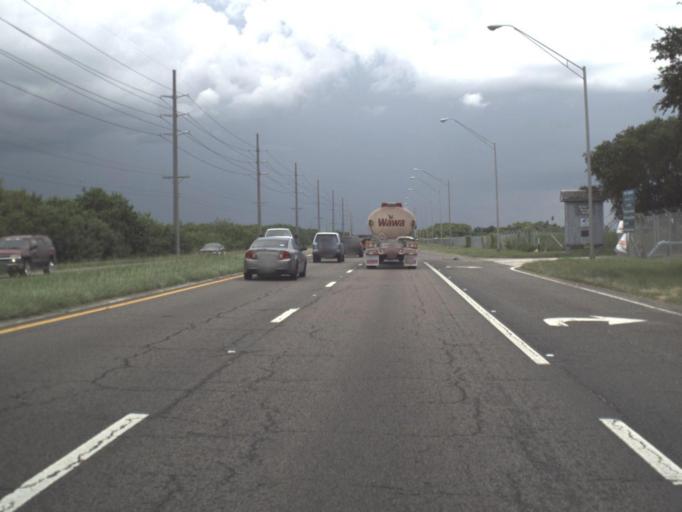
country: US
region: Florida
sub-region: Hillsborough County
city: Tampa
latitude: 27.9289
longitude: -82.4255
